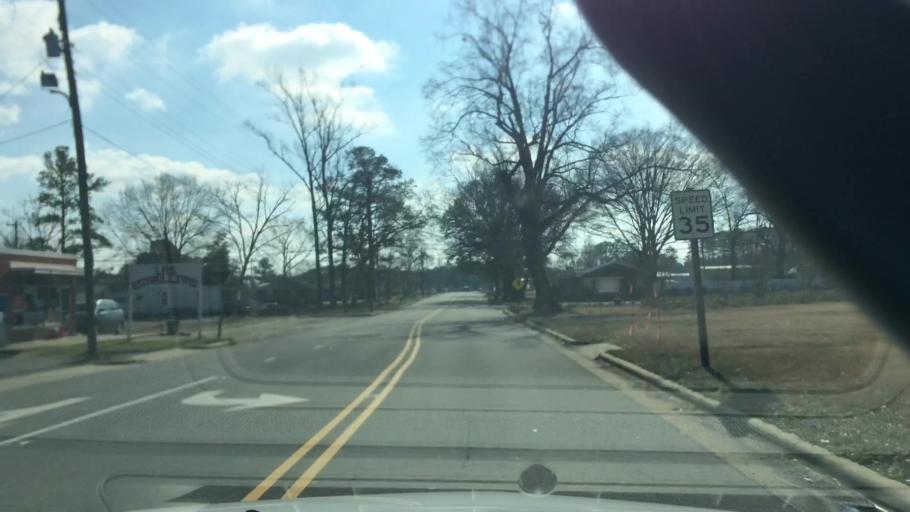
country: US
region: North Carolina
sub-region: Duplin County
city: Beulaville
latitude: 35.0548
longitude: -77.7437
